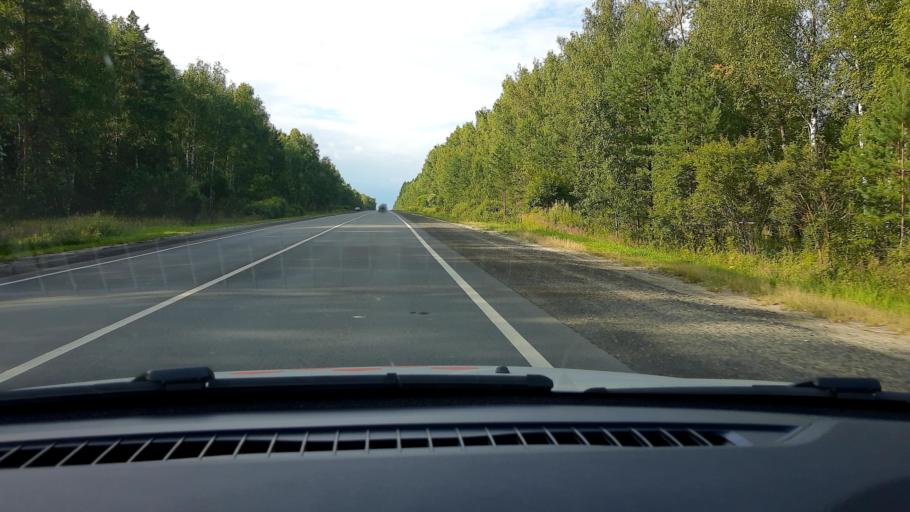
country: RU
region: Nizjnij Novgorod
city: Arzamas
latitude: 55.4936
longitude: 43.8904
